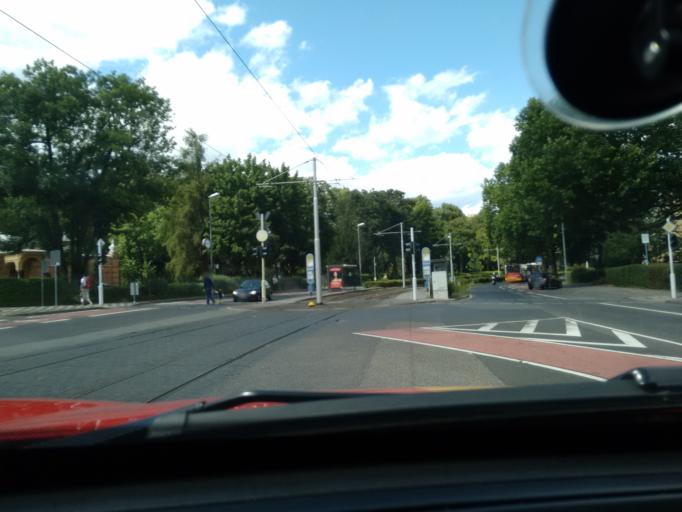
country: DE
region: Rheinland-Pfalz
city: Mainz
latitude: 49.9918
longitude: 8.2519
